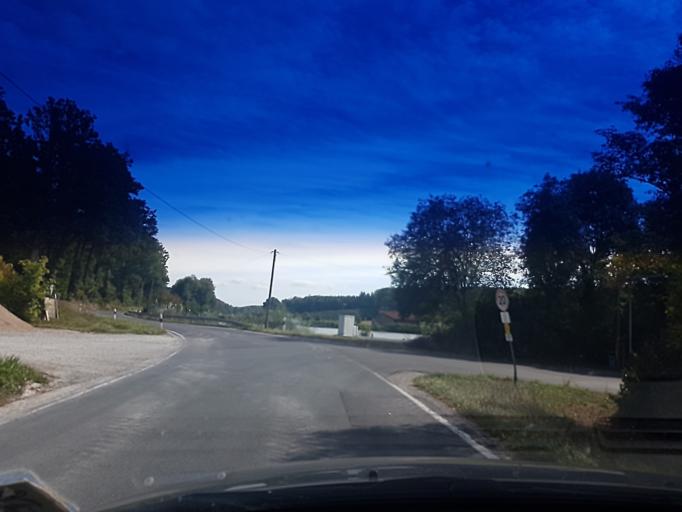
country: DE
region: Bavaria
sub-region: Regierungsbezirk Mittelfranken
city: Wachenroth
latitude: 49.7824
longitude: 10.7016
